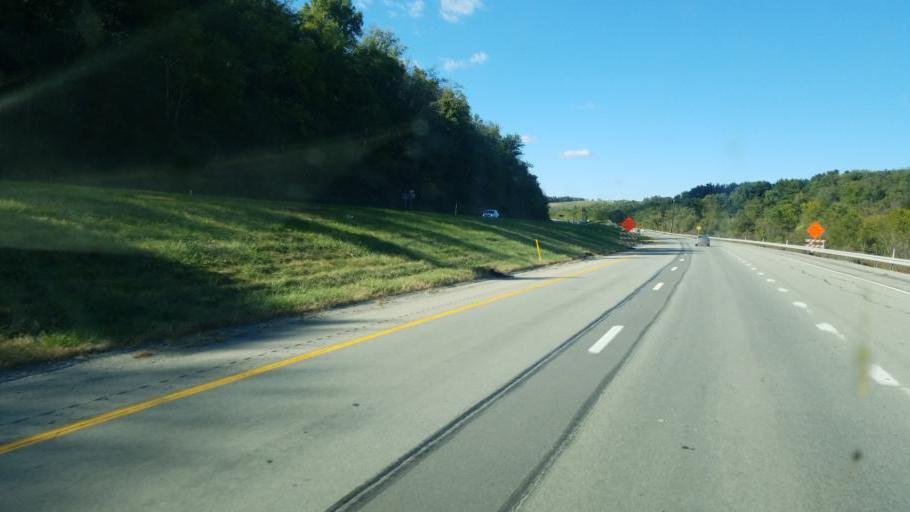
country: US
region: Pennsylvania
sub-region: Washington County
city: East Washington
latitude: 40.1152
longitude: -80.2027
